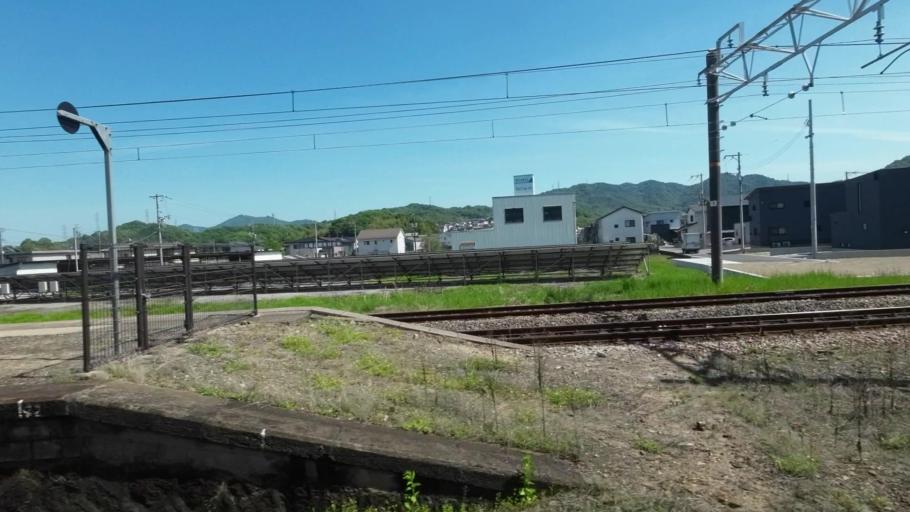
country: JP
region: Hiroshima
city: Fukuyama
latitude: 34.4716
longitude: 133.3048
